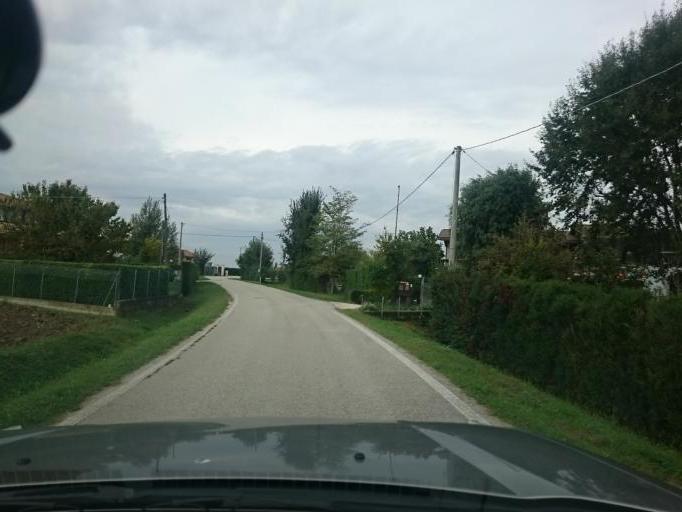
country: IT
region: Veneto
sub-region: Provincia di Padova
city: Codevigo
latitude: 45.2446
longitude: 12.0984
